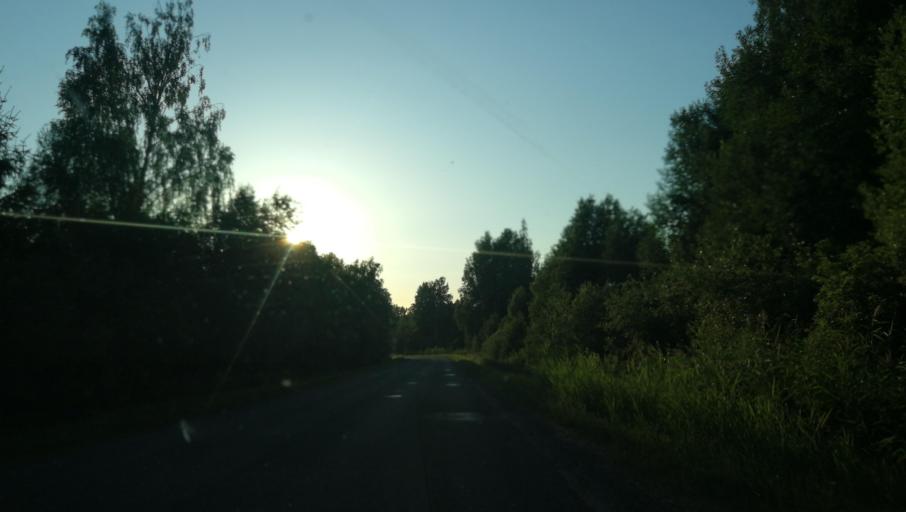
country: LV
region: Priekuli
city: Priekuli
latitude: 57.2725
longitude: 25.3353
